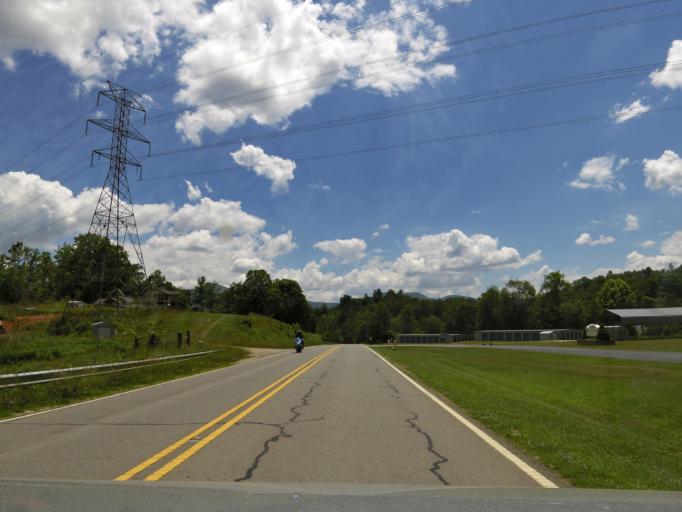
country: US
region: North Carolina
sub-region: Graham County
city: Robbinsville
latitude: 35.3359
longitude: -83.8125
